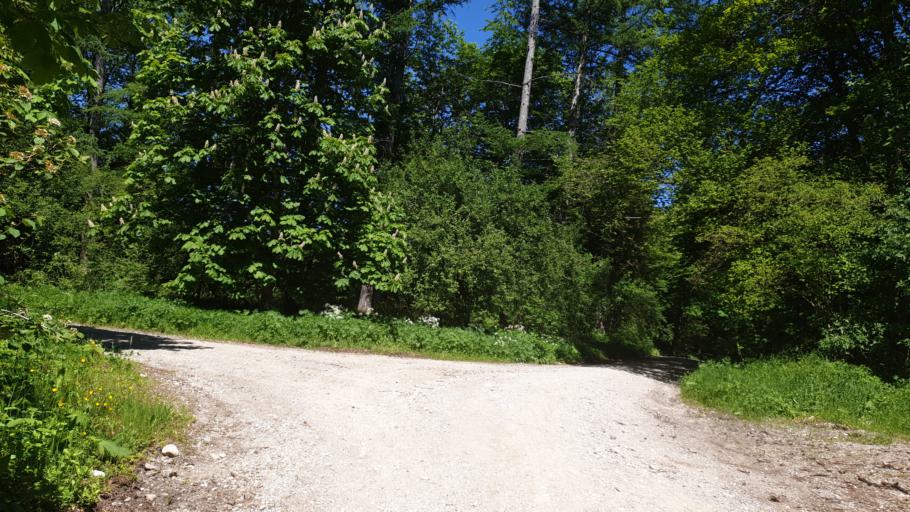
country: DE
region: Bavaria
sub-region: Upper Bavaria
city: Seeshaupt
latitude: 47.8044
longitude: 11.2862
